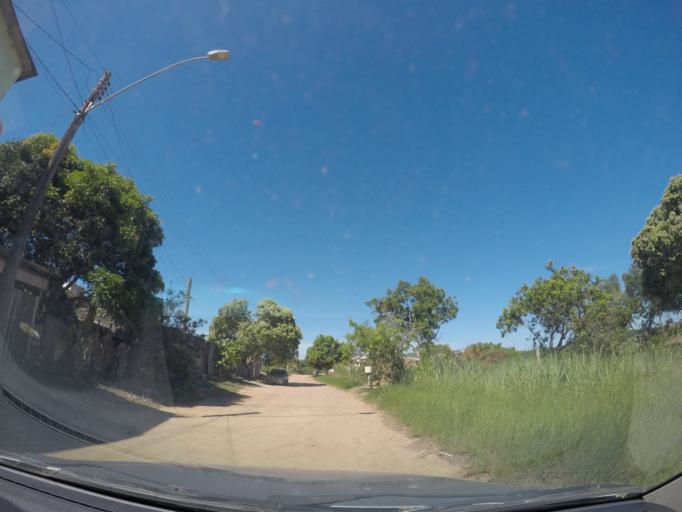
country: BR
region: Espirito Santo
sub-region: Aracruz
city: Aracruz
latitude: -19.9214
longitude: -40.1200
